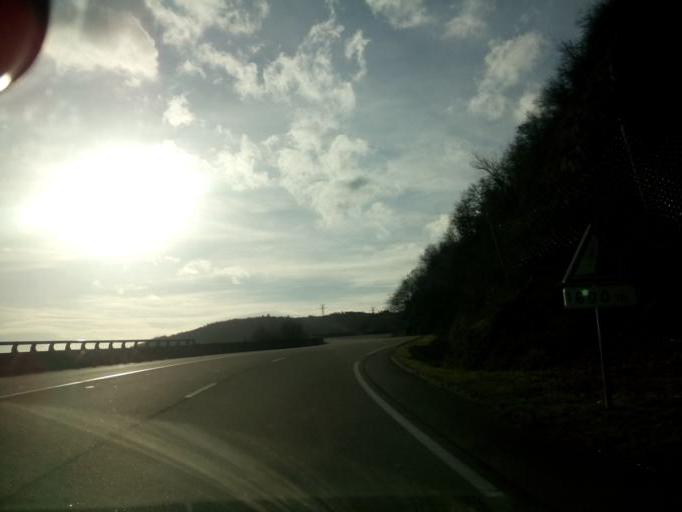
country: FR
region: Rhone-Alpes
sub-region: Departement de l'Ardeche
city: Serrieres
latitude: 45.3149
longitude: 4.7678
